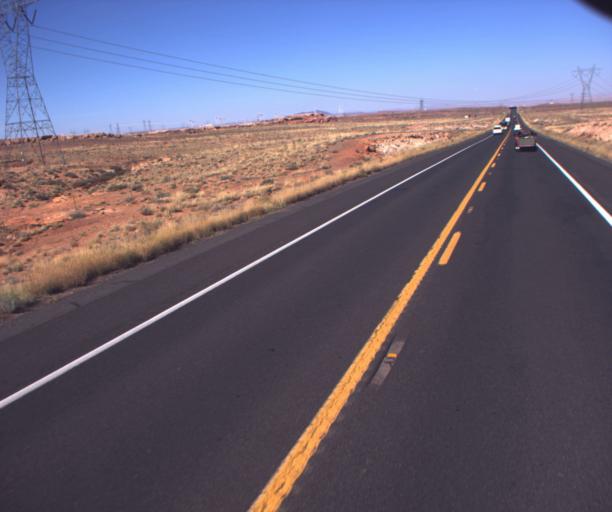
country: US
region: Arizona
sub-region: Coconino County
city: Tuba City
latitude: 35.8143
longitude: -111.4424
